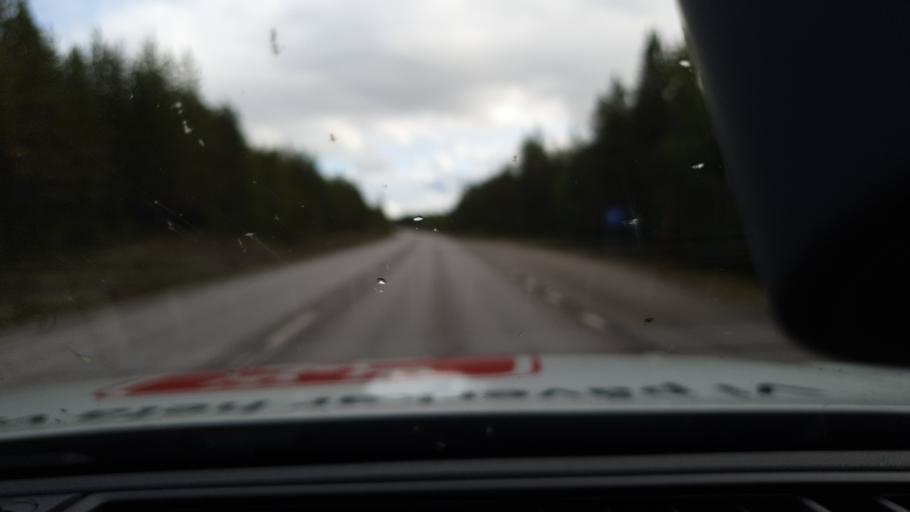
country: SE
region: Norrbotten
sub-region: Gallivare Kommun
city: Gaellivare
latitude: 67.1125
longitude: 20.7900
